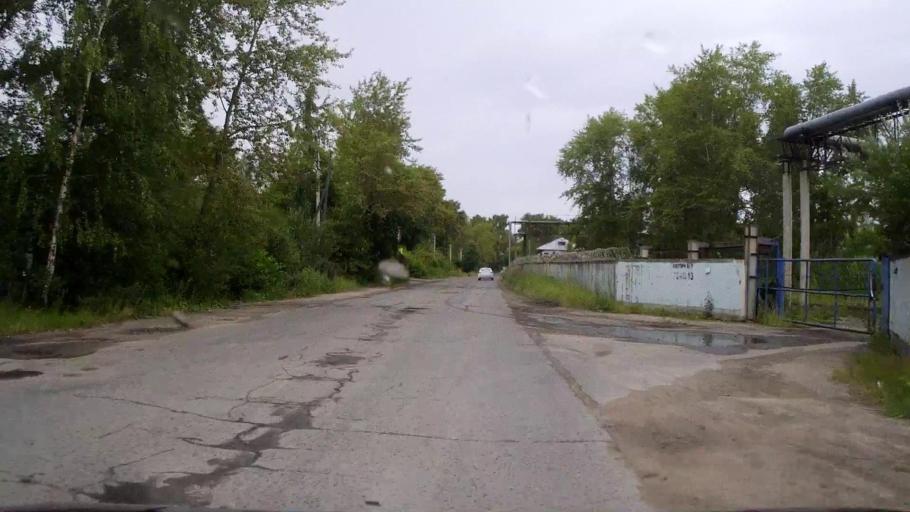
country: RU
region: Vologda
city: Vologda
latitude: 59.2029
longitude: 39.8767
